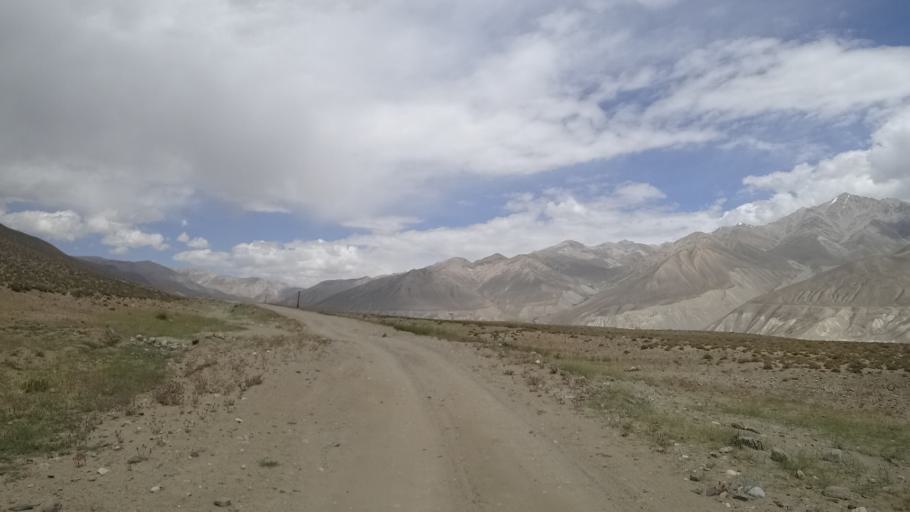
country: AF
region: Badakhshan
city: Khandud
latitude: 37.1319
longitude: 72.7323
